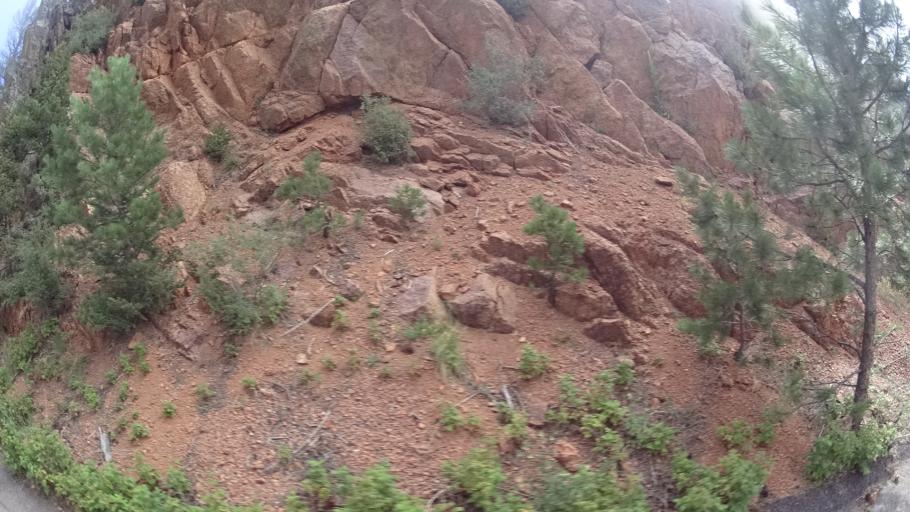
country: US
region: Colorado
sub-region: El Paso County
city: Cascade-Chipita Park
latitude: 38.8985
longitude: -104.9872
